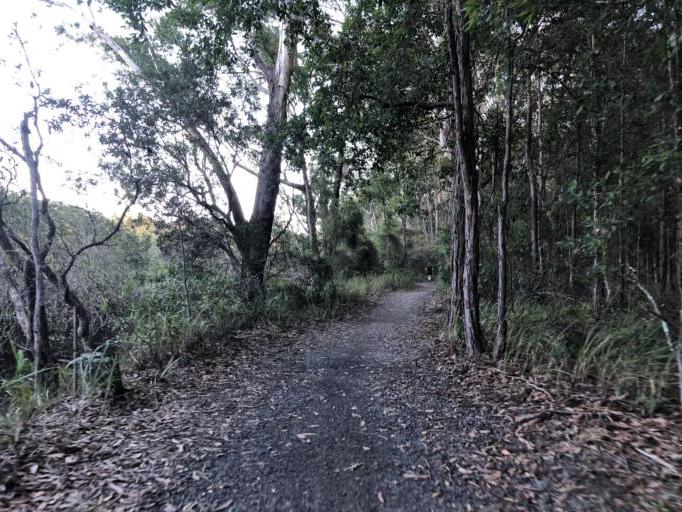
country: AU
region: New South Wales
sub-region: Coffs Harbour
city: Coffs Harbour
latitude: -30.3037
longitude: 153.1305
